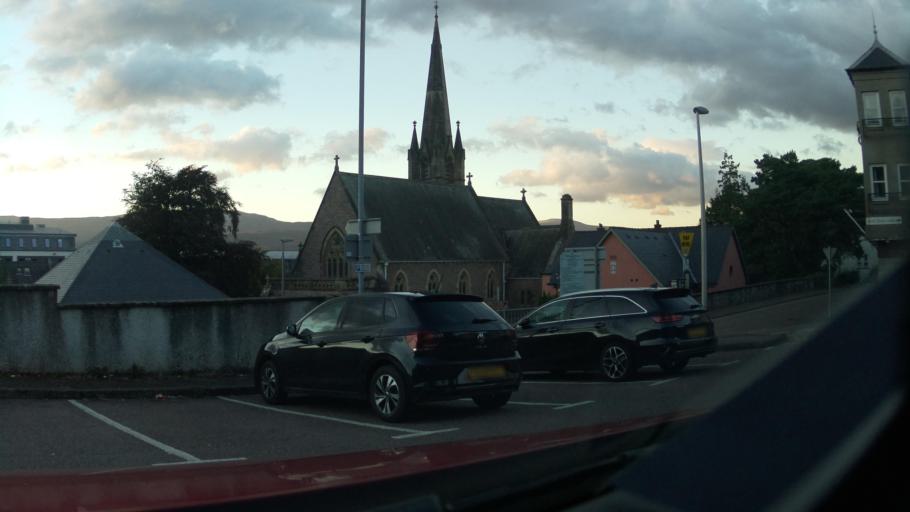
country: GB
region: Scotland
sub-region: Highland
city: Fort William
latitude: 56.8181
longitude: -5.1090
